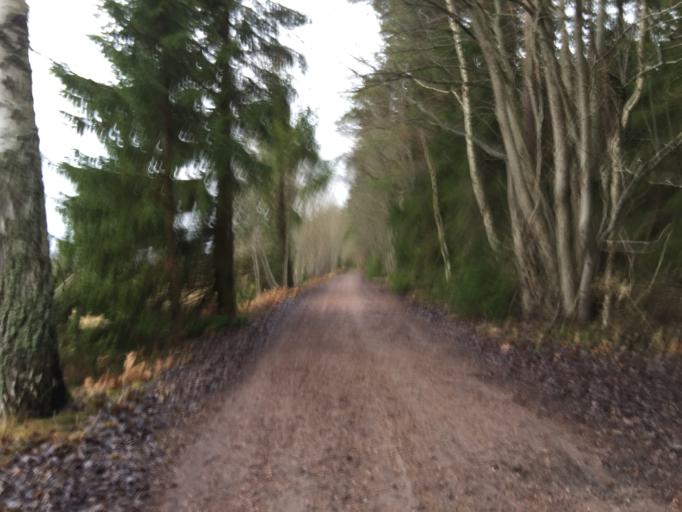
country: SE
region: Uppsala
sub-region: Osthammars Kommun
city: Bjorklinge
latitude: 60.0438
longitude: 17.5430
